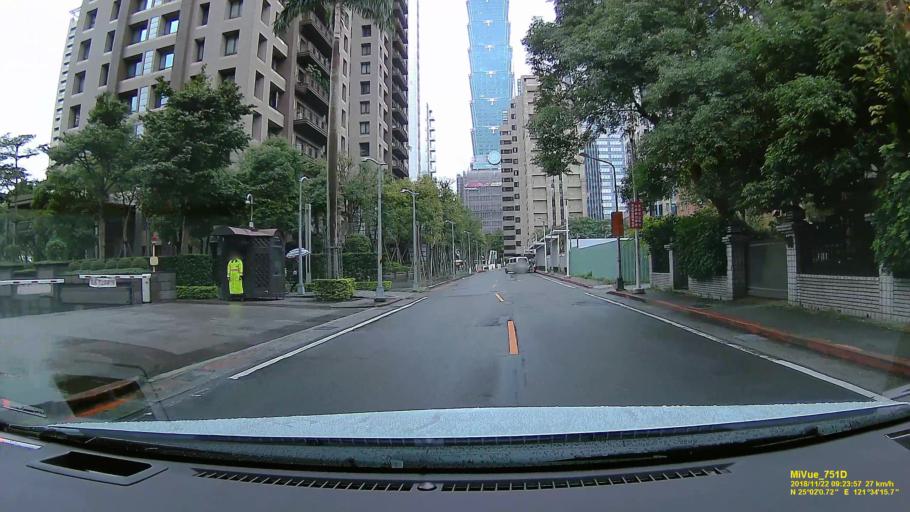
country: TW
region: Taipei
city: Taipei
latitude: 25.0336
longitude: 121.5709
